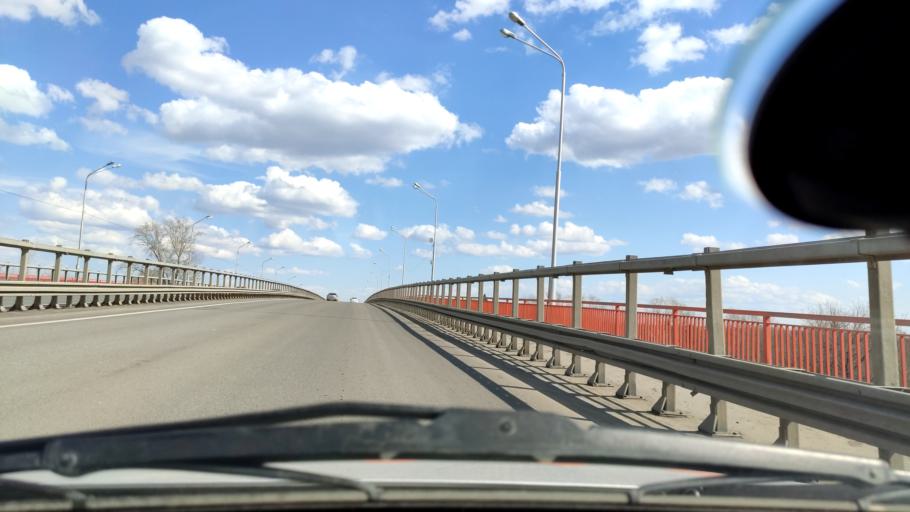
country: RU
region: Bashkortostan
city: Ufa
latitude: 54.8029
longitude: 56.1414
